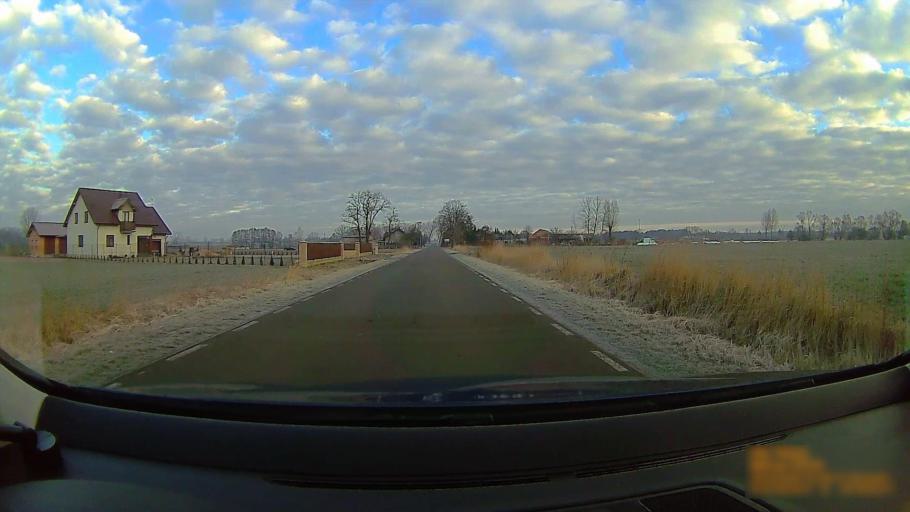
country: PL
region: Greater Poland Voivodeship
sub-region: Powiat koninski
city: Rzgow Pierwszy
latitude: 52.1424
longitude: 18.0560
